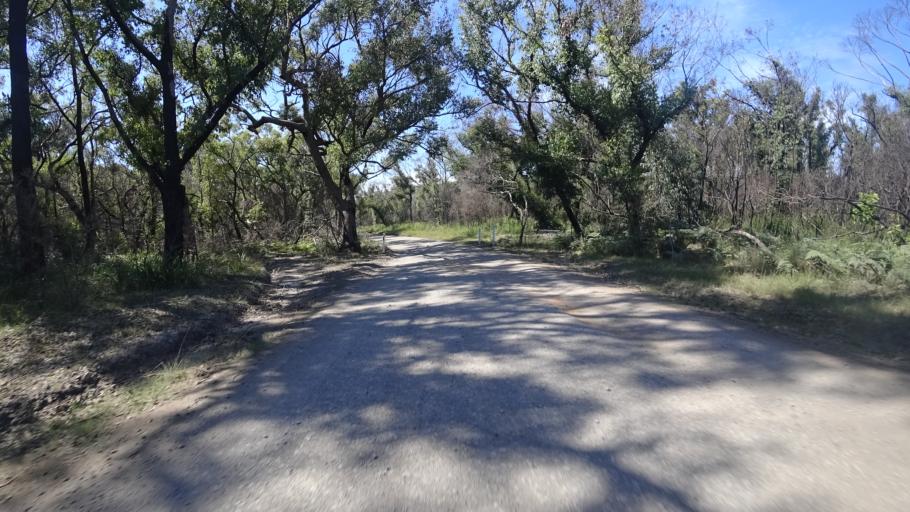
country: AU
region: New South Wales
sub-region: Shoalhaven Shire
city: Falls Creek
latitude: -35.1544
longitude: 150.7114
